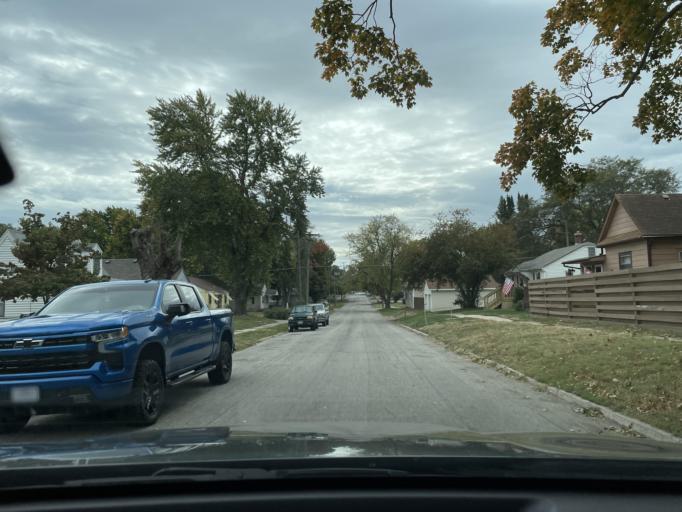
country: US
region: Missouri
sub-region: Buchanan County
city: Saint Joseph
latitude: 39.7702
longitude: -94.8224
